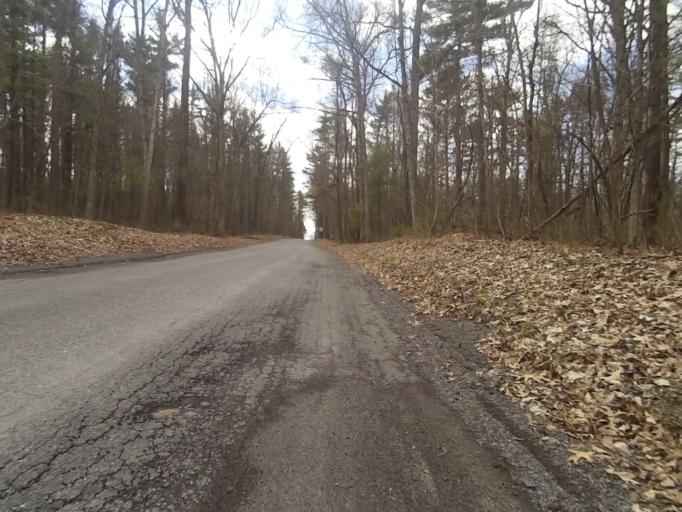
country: US
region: Pennsylvania
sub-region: Centre County
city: Houserville
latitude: 40.8694
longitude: -77.8167
